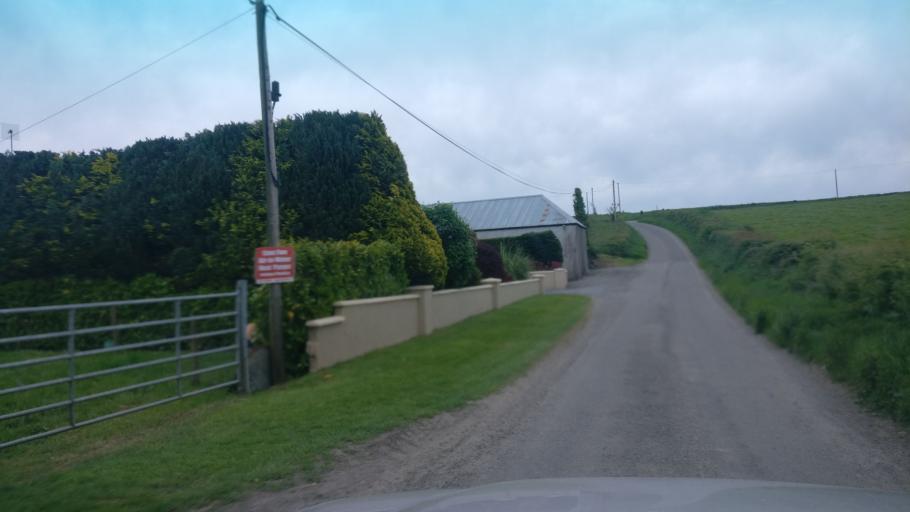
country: IE
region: Connaught
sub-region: County Galway
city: Portumna
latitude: 53.1332
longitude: -8.2919
